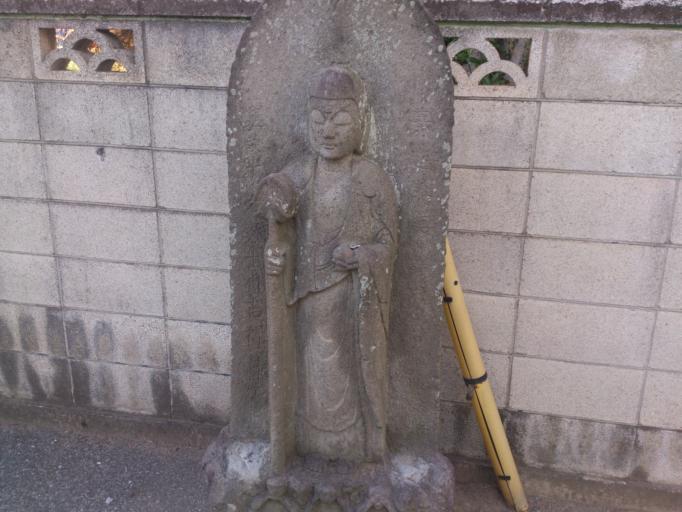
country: JP
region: Chiba
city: Matsudo
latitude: 35.7945
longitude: 139.8938
